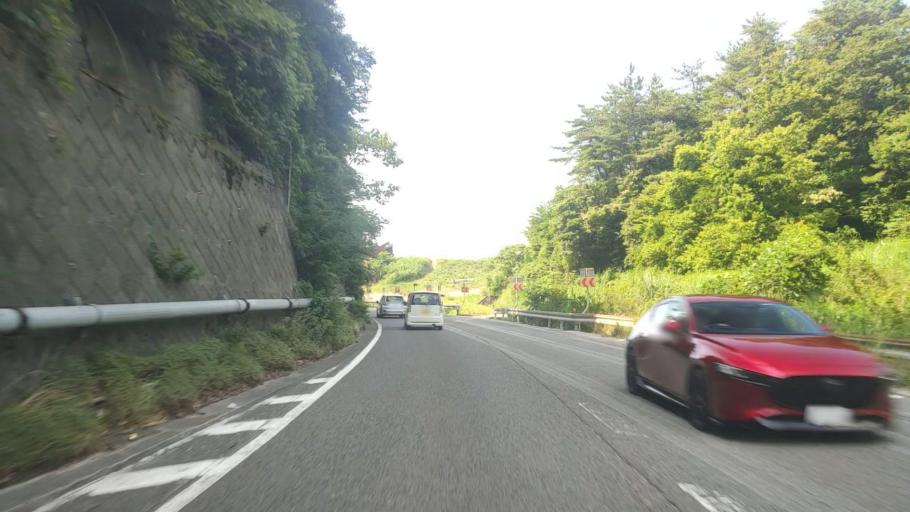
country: JP
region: Fukui
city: Tsuruga
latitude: 35.5724
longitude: 136.1234
